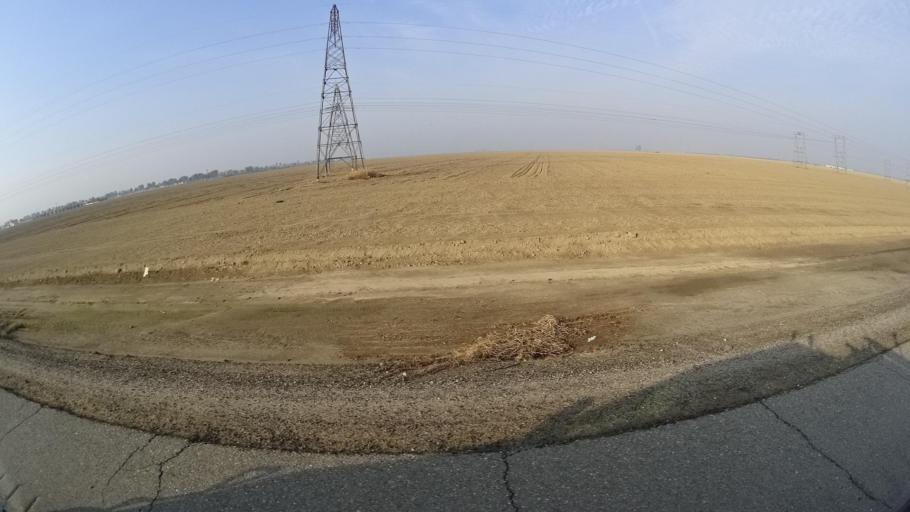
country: US
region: California
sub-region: Kern County
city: Weedpatch
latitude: 35.1834
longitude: -118.9146
